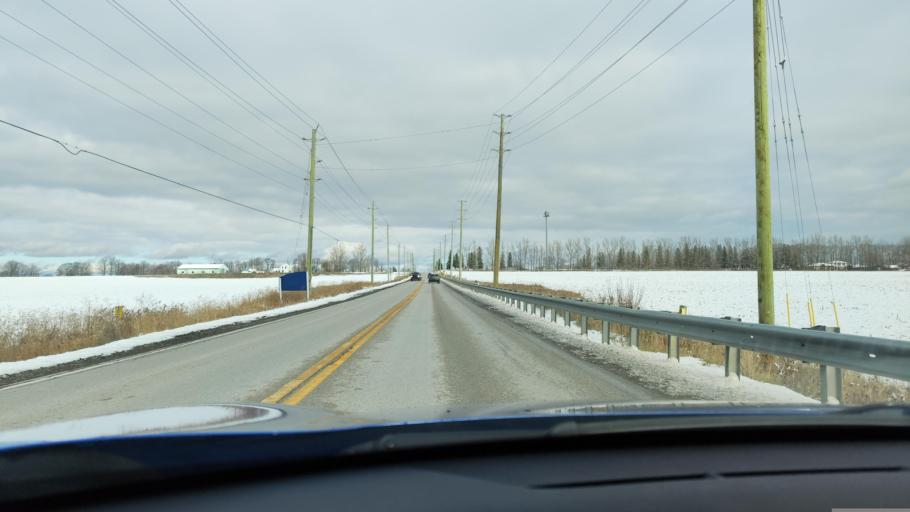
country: CA
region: Ontario
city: Barrie
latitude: 44.3924
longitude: -79.7529
